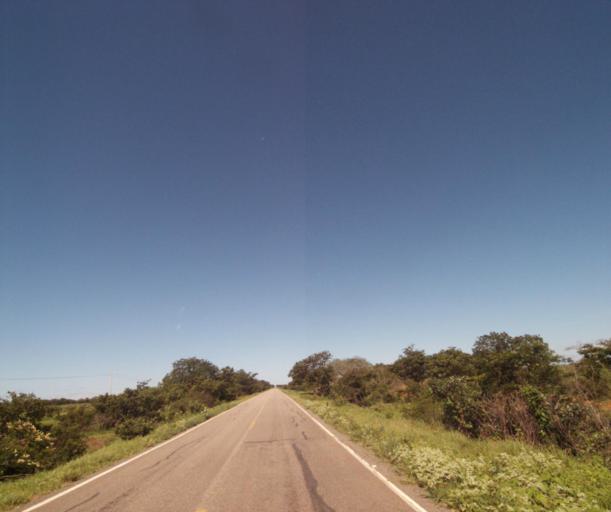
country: BR
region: Bahia
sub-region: Palmas De Monte Alto
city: Palmas de Monte Alto
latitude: -14.2629
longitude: -43.3261
